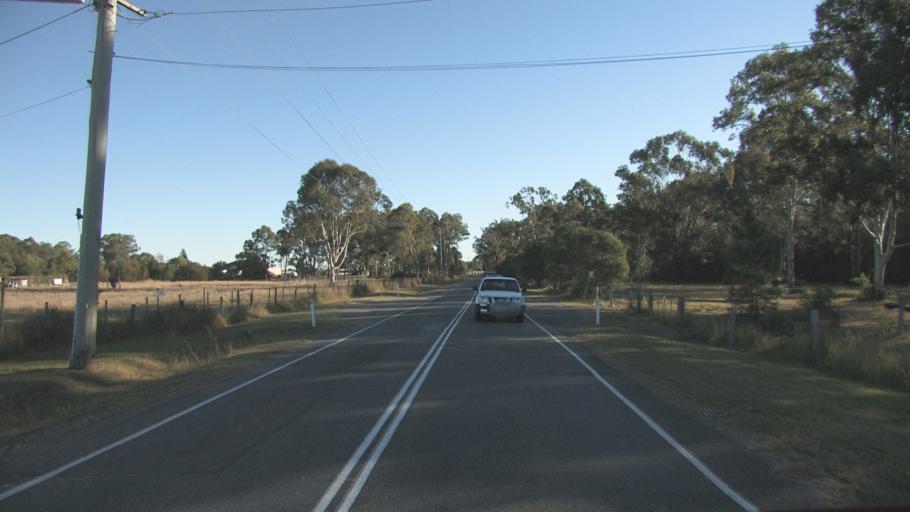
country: AU
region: Queensland
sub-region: Logan
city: Chambers Flat
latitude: -27.7535
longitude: 153.0913
